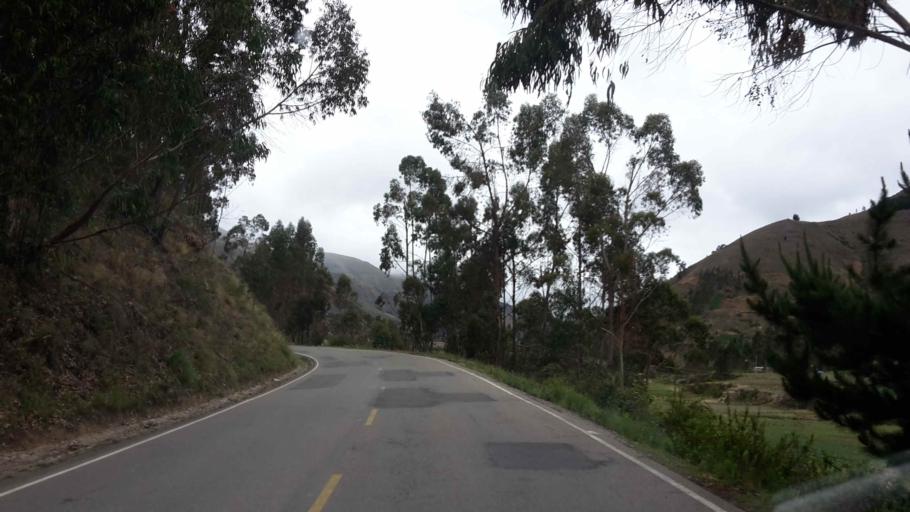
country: BO
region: Cochabamba
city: Arani
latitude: -17.4779
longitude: -65.5346
